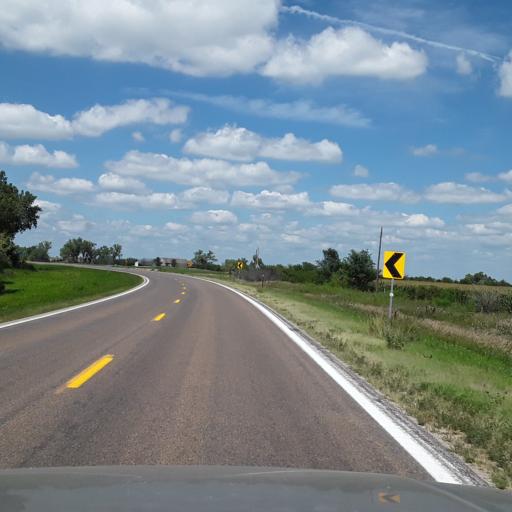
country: US
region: Nebraska
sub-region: Nance County
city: Genoa
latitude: 41.3311
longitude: -97.6755
